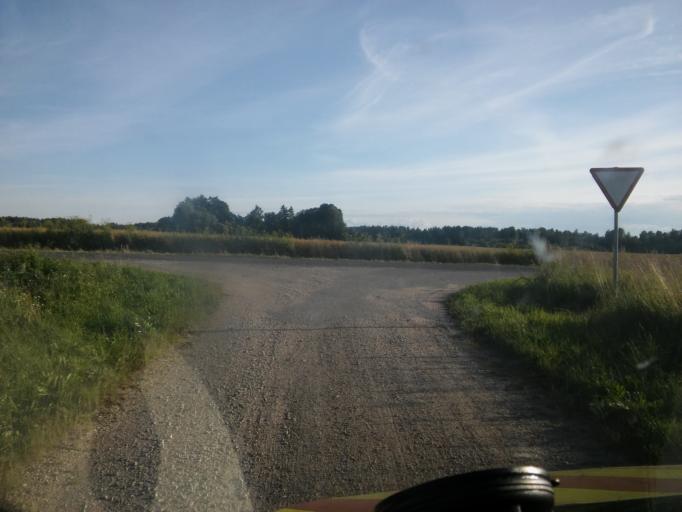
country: EE
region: Valgamaa
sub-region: Torva linn
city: Torva
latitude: 58.0779
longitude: 25.9907
